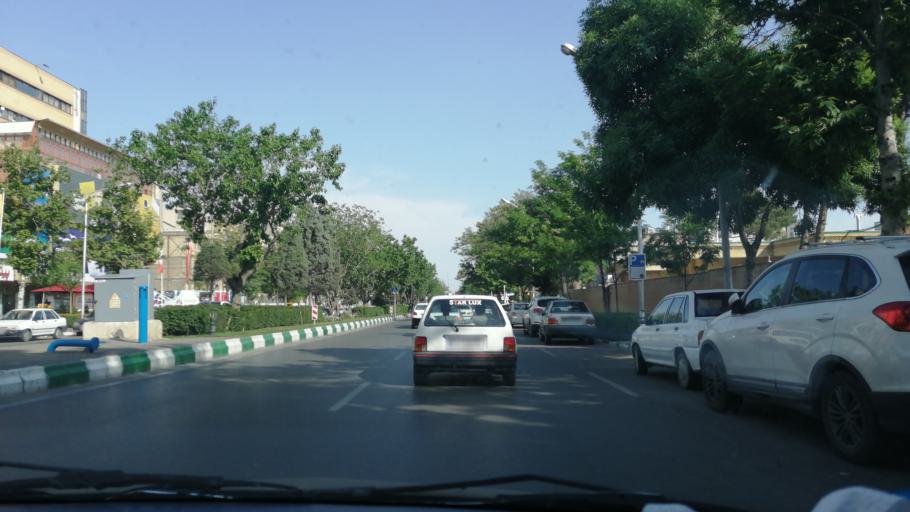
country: IR
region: Razavi Khorasan
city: Mashhad
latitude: 36.3135
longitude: 59.5620
